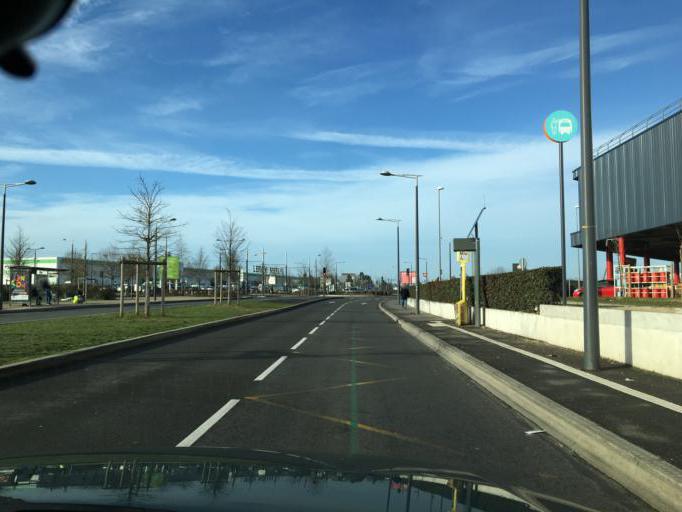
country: FR
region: Centre
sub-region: Departement du Loiret
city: Saint-Jean-de-la-Ruelle
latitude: 47.9026
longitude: 1.8606
